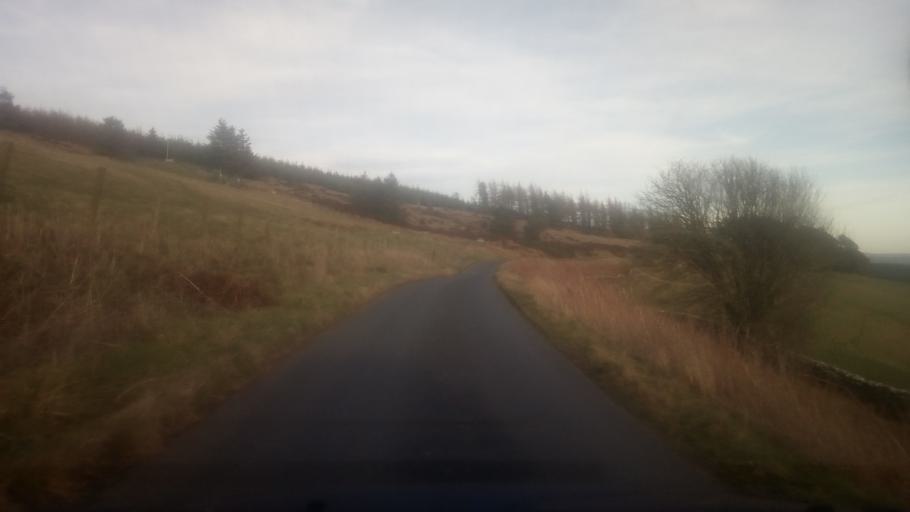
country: GB
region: Scotland
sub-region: The Scottish Borders
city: Jedburgh
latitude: 55.3936
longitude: -2.5730
